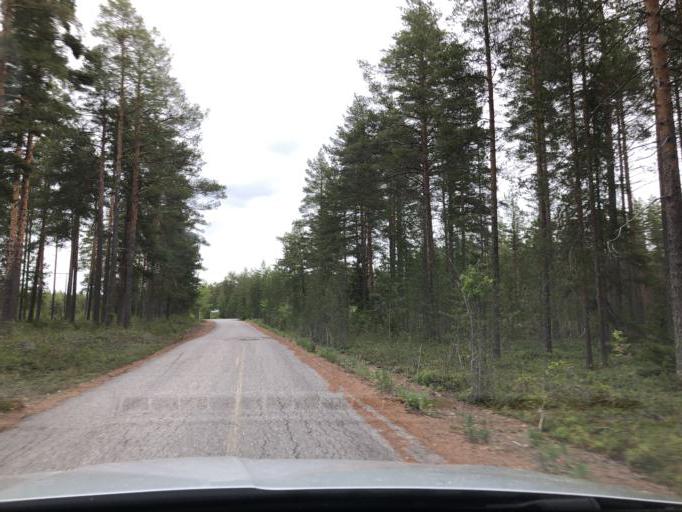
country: SE
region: Norrbotten
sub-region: Pitea Kommun
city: Pitea
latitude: 65.2370
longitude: 21.5174
